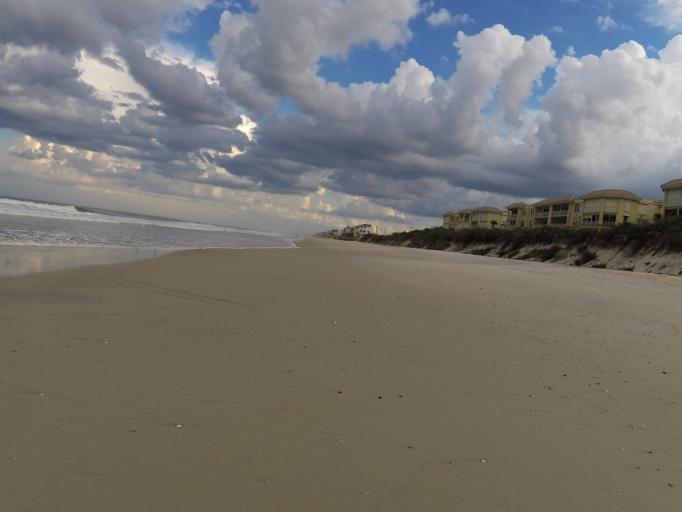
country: US
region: Florida
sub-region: Saint Johns County
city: Villano Beach
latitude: 29.9683
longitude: -81.3087
